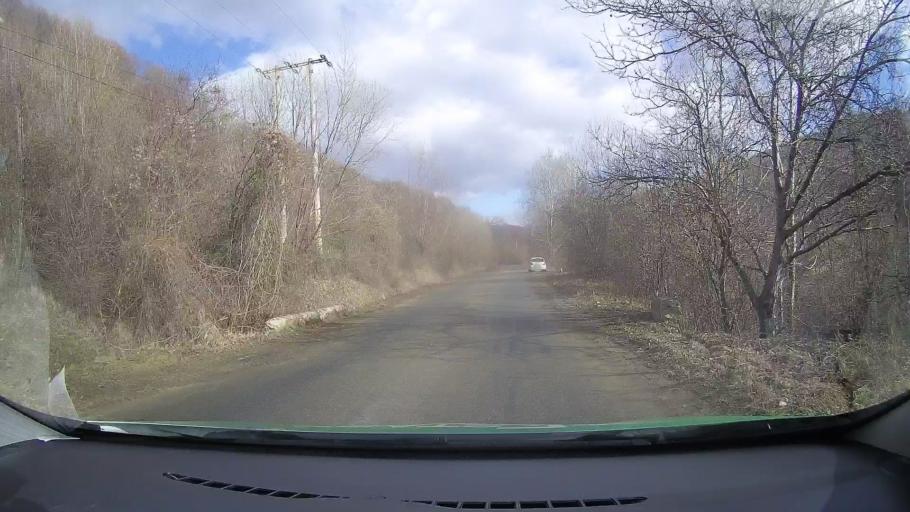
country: RO
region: Dambovita
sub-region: Comuna Motaeni
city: Motaeni
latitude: 45.1035
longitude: 25.4404
